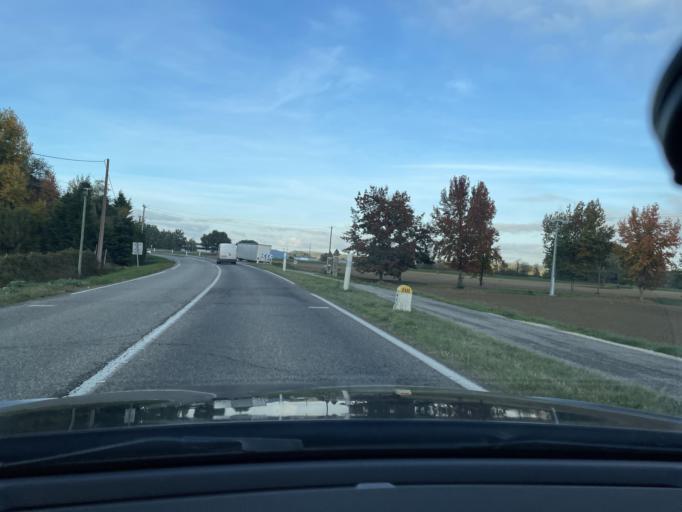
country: FR
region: Aquitaine
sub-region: Departement du Lot-et-Garonne
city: Fourques-sur-Garonne
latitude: 44.4038
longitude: 0.1243
